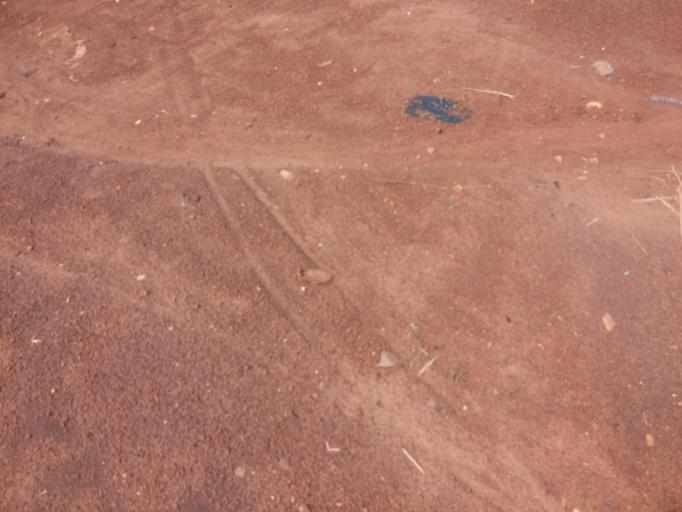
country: TG
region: Centrale
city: Sotouboua
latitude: 8.5598
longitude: 0.9840
